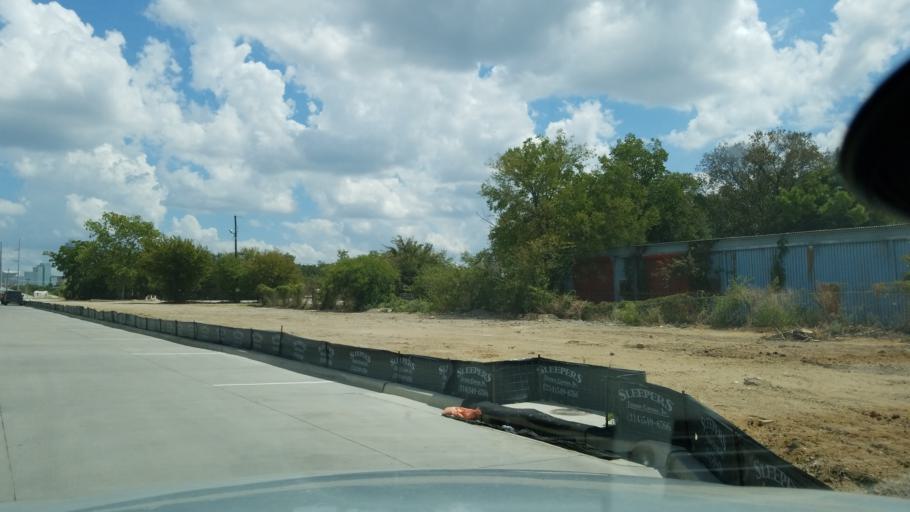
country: US
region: Texas
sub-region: Dallas County
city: Dallas
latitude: 32.7774
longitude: -96.8321
